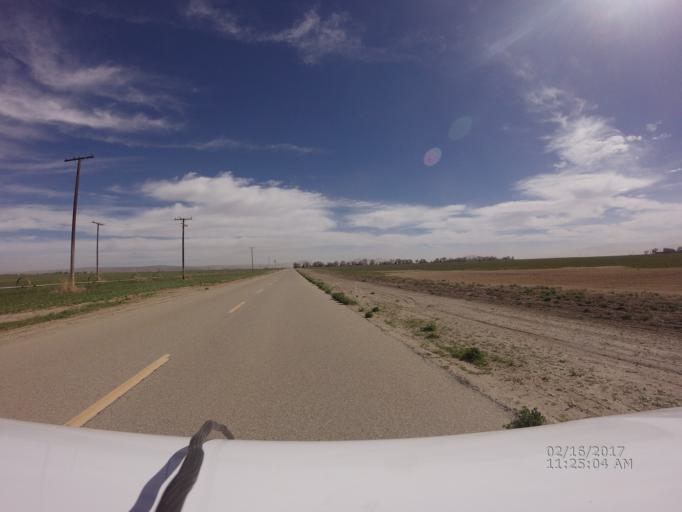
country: US
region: California
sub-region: Los Angeles County
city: Lake Los Angeles
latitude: 34.7047
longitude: -117.9303
